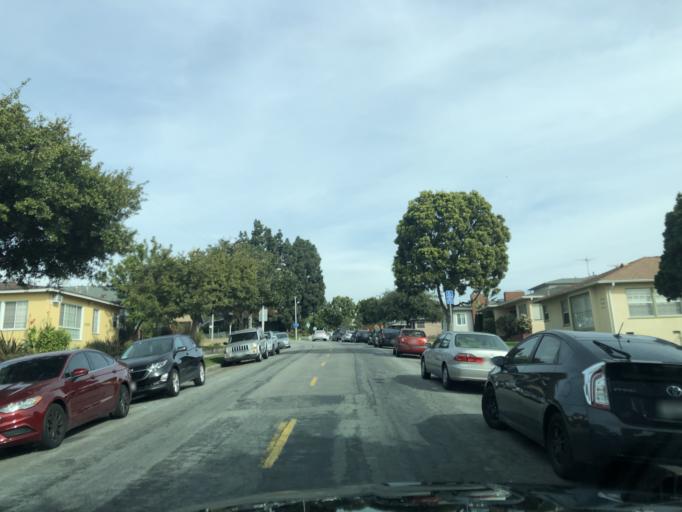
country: US
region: California
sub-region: Los Angeles County
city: Ladera Heights
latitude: 33.9848
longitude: -118.3655
